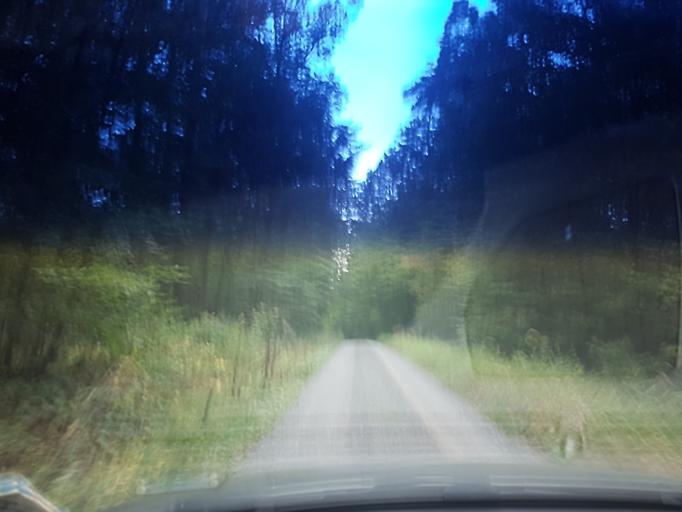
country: DE
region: Bavaria
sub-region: Upper Franconia
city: Burgwindheim
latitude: 49.8608
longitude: 10.5150
